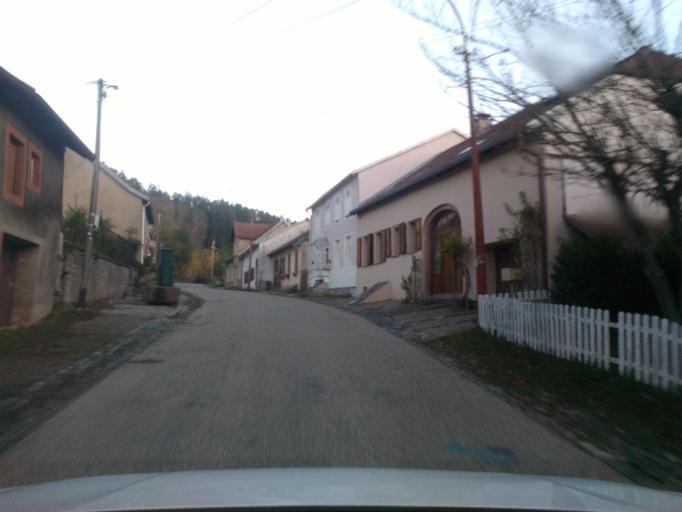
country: FR
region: Lorraine
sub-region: Departement des Vosges
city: Ban-de-Laveline
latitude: 48.3509
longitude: 7.1066
